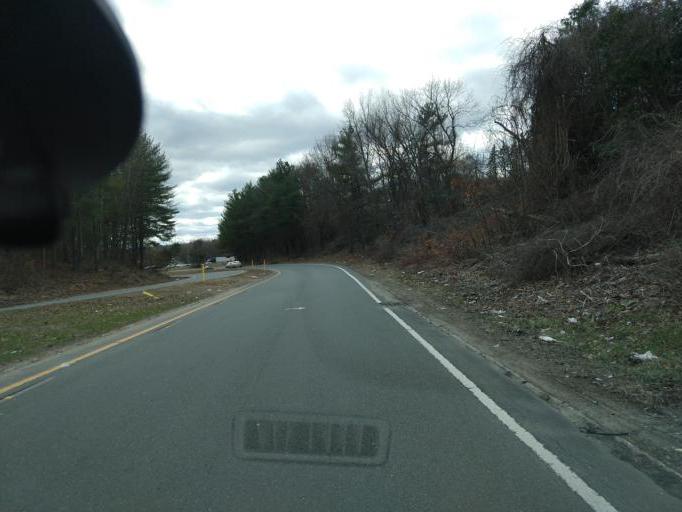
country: US
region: Massachusetts
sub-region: Essex County
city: Haverhill
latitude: 42.8015
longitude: -71.0953
